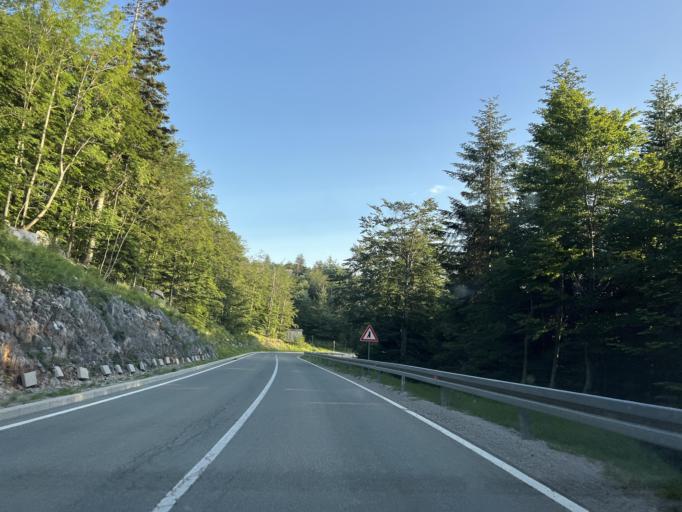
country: HR
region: Primorsko-Goranska
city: Podhum
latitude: 45.4133
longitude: 14.5615
